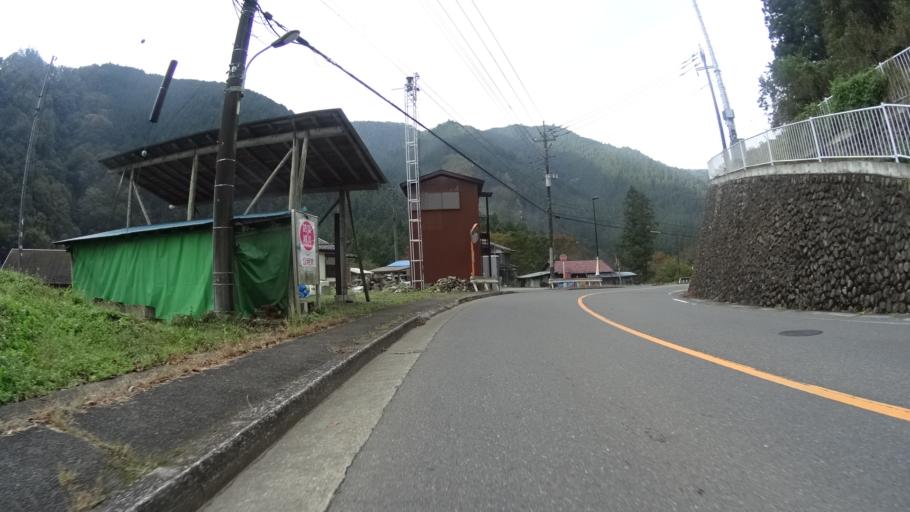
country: JP
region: Tokyo
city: Itsukaichi
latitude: 35.7030
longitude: 139.1419
